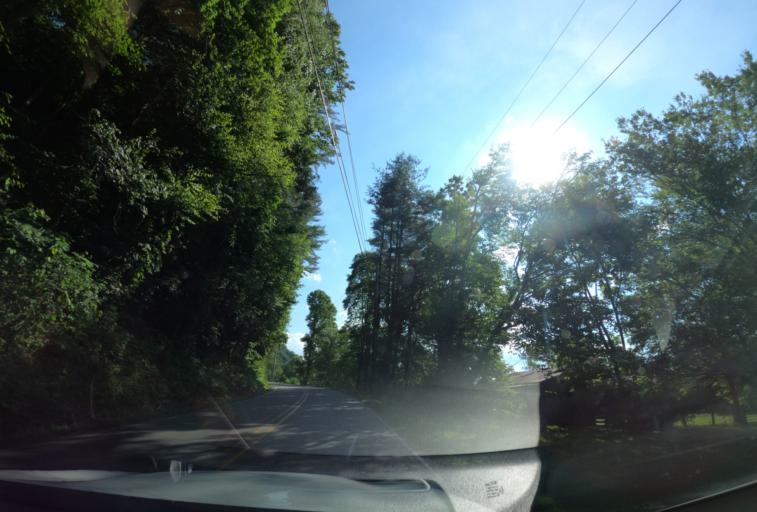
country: US
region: North Carolina
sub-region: Transylvania County
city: Brevard
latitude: 35.2549
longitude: -82.6713
